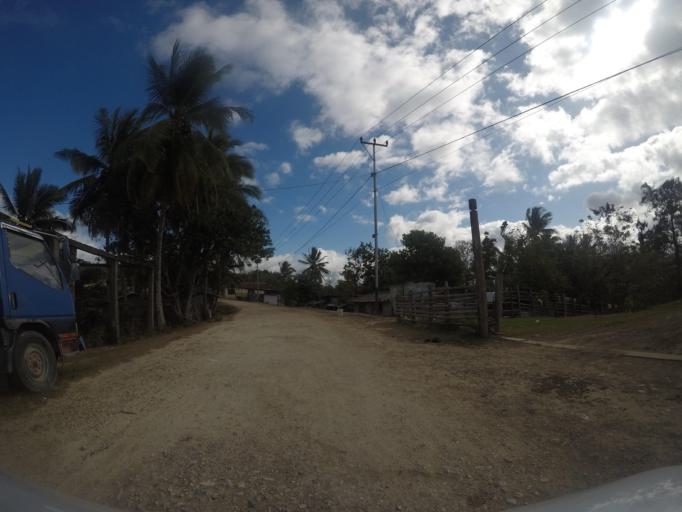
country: TL
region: Lautem
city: Lospalos
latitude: -8.5689
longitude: 126.8842
